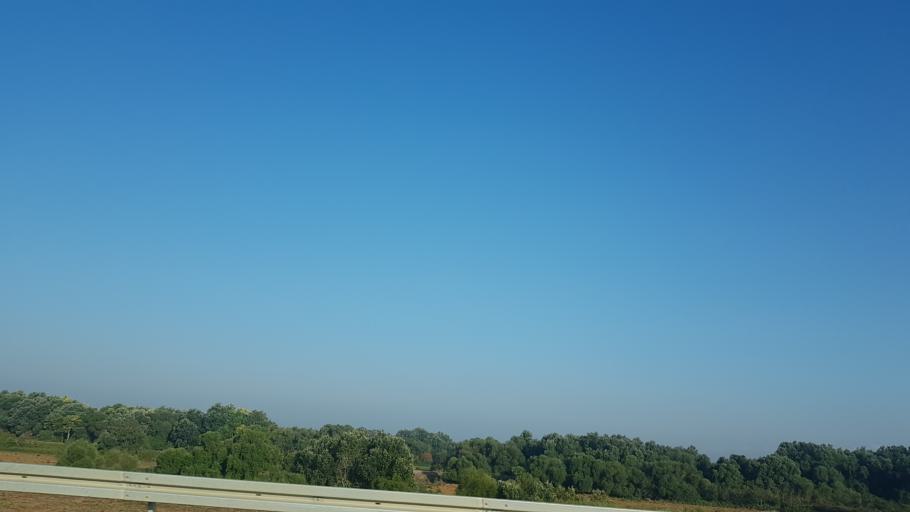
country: TR
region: Bursa
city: Karacabey
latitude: 40.1658
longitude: 28.3191
